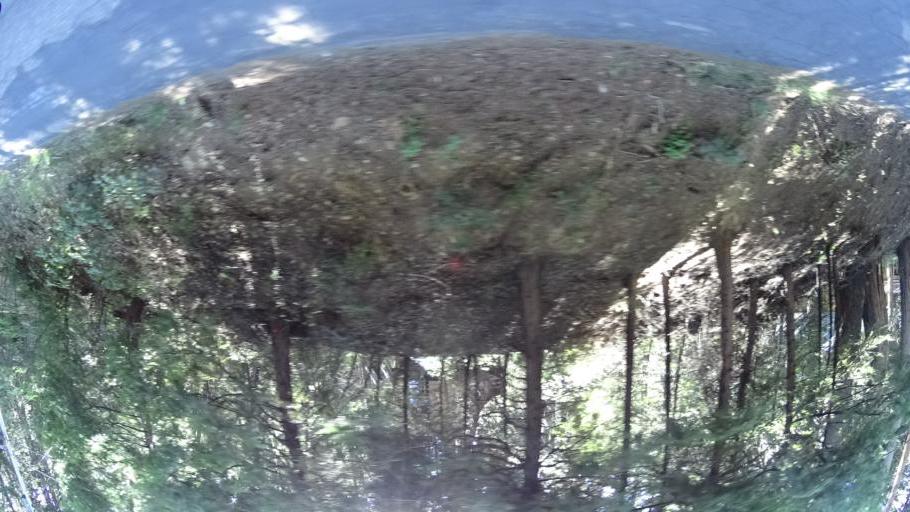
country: US
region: California
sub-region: Calaveras County
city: Arnold
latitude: 38.2994
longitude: -120.2729
